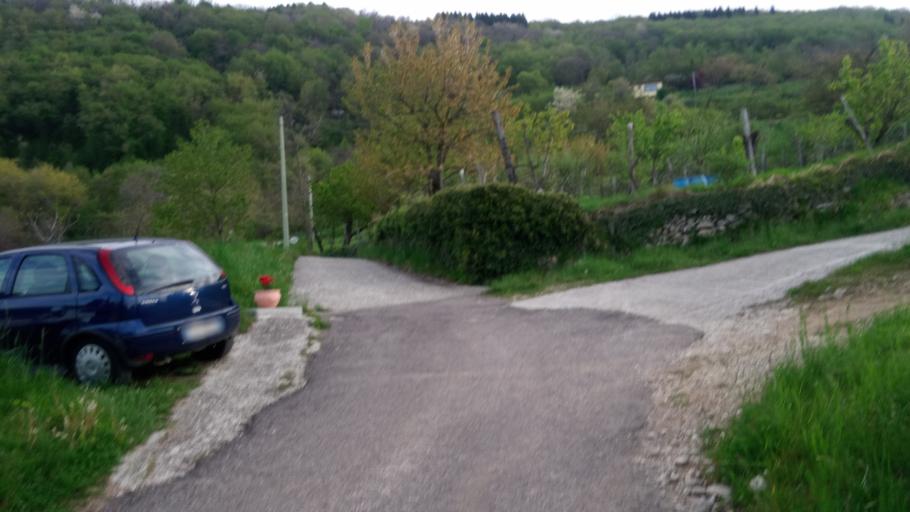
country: IT
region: Veneto
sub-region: Provincia di Vicenza
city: Conco
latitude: 45.7768
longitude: 11.6083
